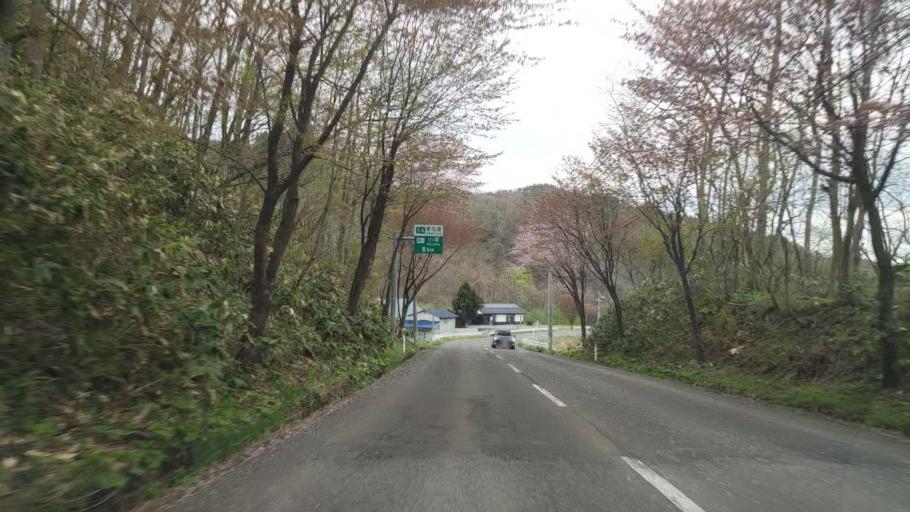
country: JP
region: Akita
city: Hanawa
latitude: 40.3603
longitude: 140.7852
